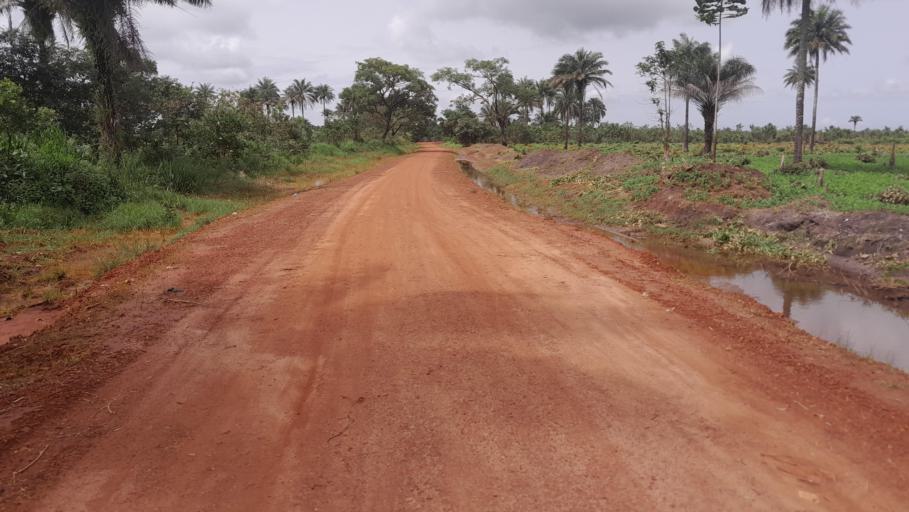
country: GN
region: Boke
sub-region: Boffa
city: Boffa
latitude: 10.0697
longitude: -13.8674
